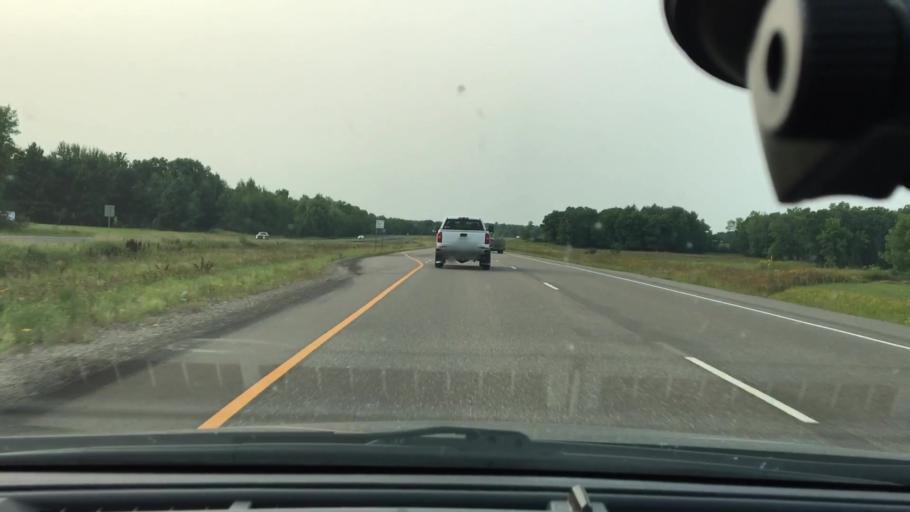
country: US
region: Minnesota
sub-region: Mille Lacs County
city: Milaca
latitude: 45.8254
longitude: -93.6571
